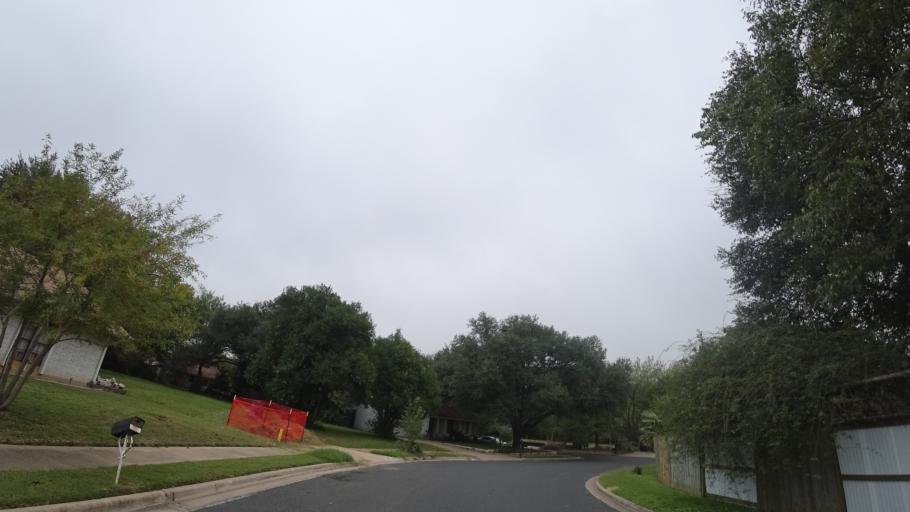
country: US
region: Texas
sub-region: Travis County
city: Austin
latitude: 30.2132
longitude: -97.7735
